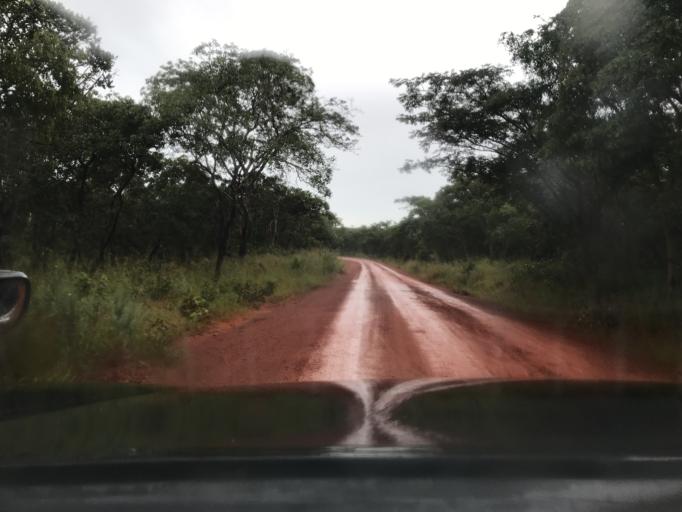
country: TZ
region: Kigoma
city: Uvinza
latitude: -5.2929
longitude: 30.3692
